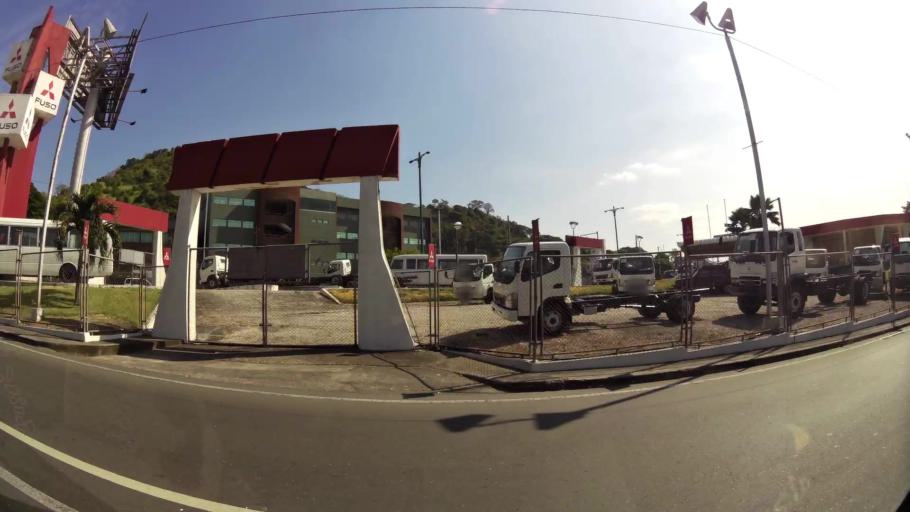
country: EC
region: Guayas
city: Guayaquil
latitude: -2.1636
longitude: -79.9241
